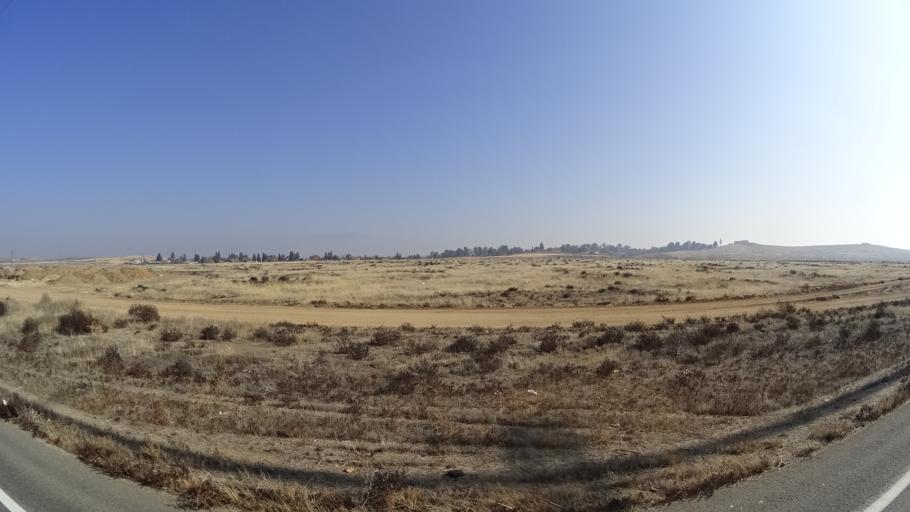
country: US
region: California
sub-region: Kern County
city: Oildale
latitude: 35.4038
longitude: -118.8788
